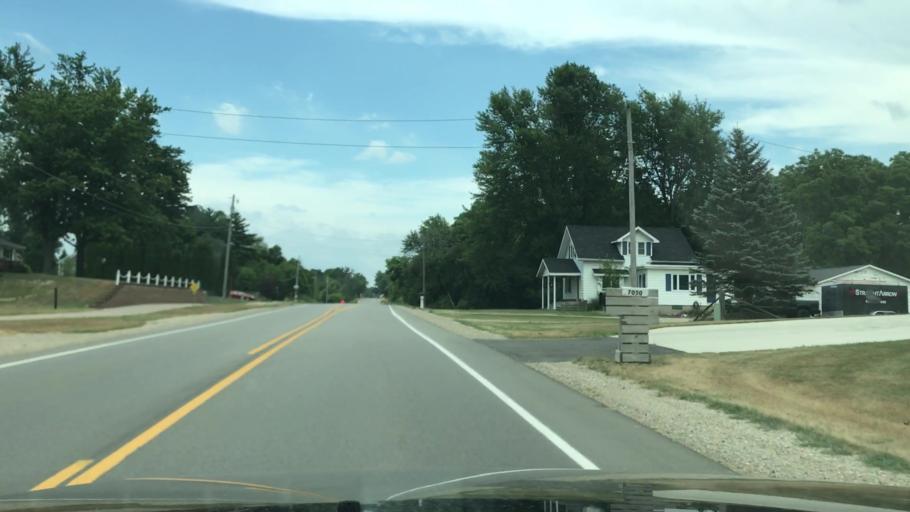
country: US
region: Michigan
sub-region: Ottawa County
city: Zeeland
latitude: 42.7831
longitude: -85.9565
